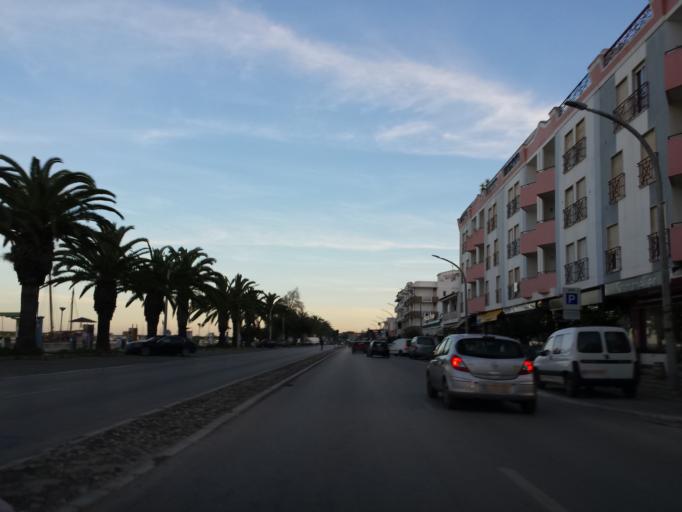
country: PT
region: Faro
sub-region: Lagos
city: Lagos
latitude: 37.1069
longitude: -8.6748
